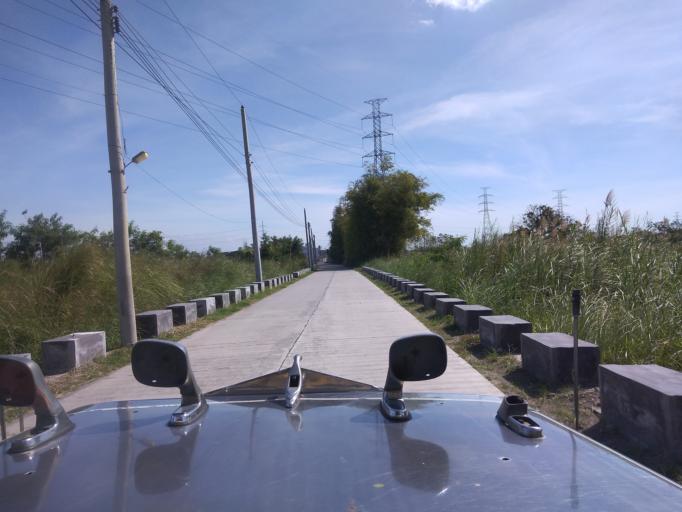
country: PH
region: Central Luzon
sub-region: Province of Pampanga
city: San Juan
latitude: 15.0249
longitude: 120.6670
